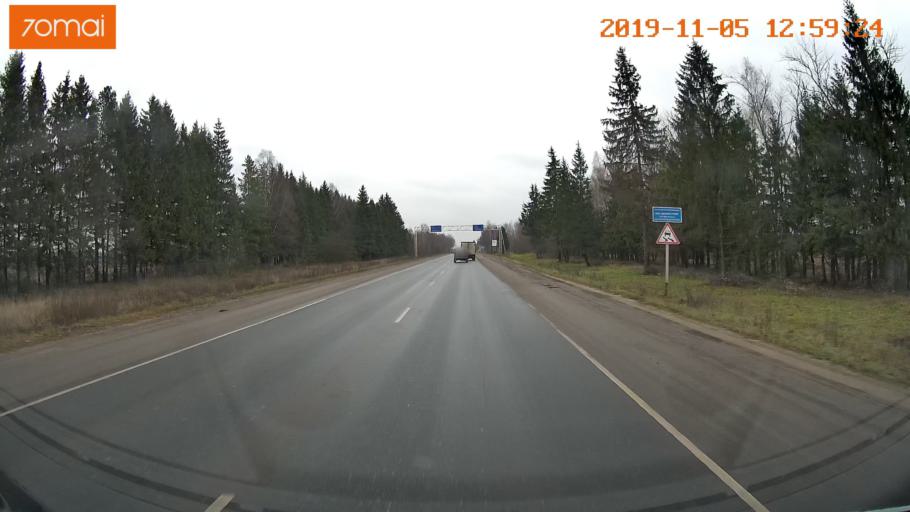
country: RU
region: Ivanovo
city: Kokhma
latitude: 56.9187
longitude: 41.1284
